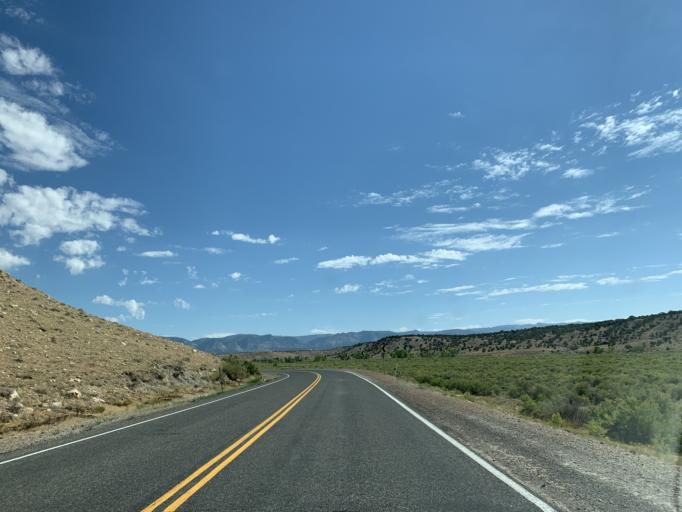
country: US
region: Utah
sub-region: Carbon County
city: Wellington
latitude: 39.5811
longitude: -110.6500
